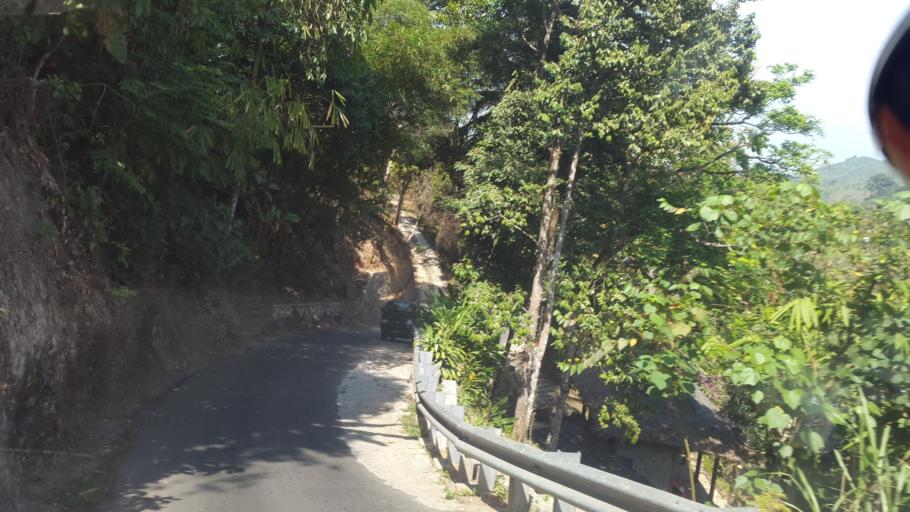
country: ID
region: West Java
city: Bojonggaling
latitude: -6.9146
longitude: 106.6124
